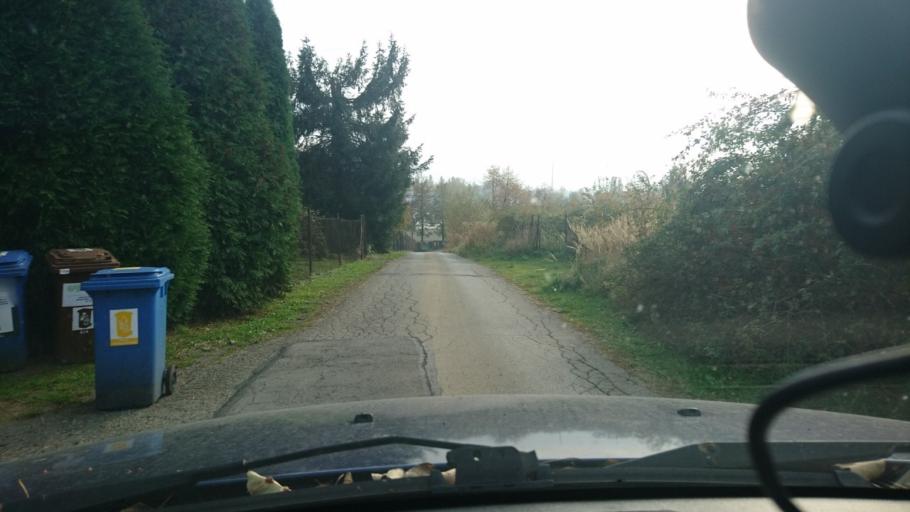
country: PL
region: Silesian Voivodeship
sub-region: Bielsko-Biala
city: Bielsko-Biala
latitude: 49.8362
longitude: 19.0658
